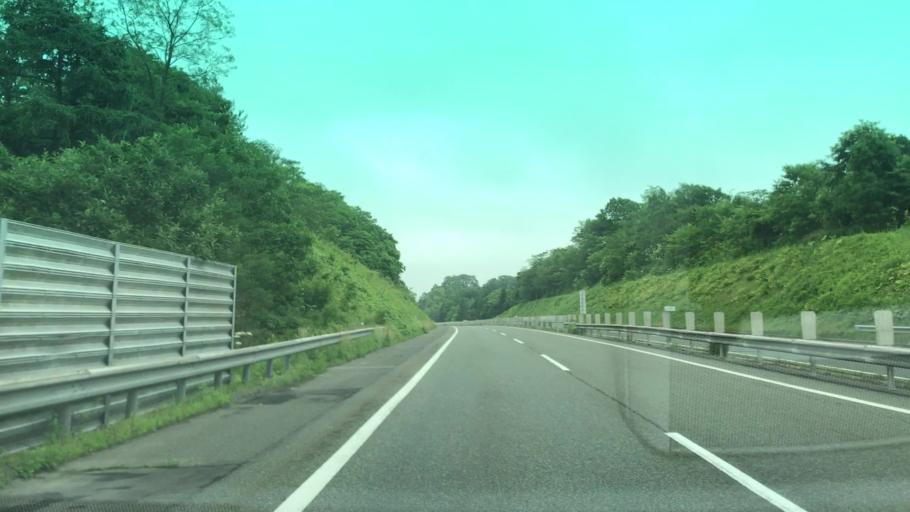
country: JP
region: Hokkaido
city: Tomakomai
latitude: 42.6523
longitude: 141.5593
